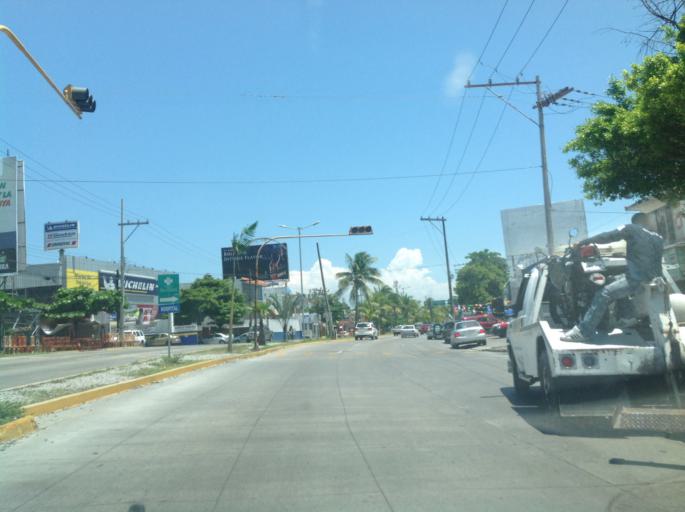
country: MX
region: Veracruz
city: Veracruz
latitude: 19.1451
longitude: -96.1264
